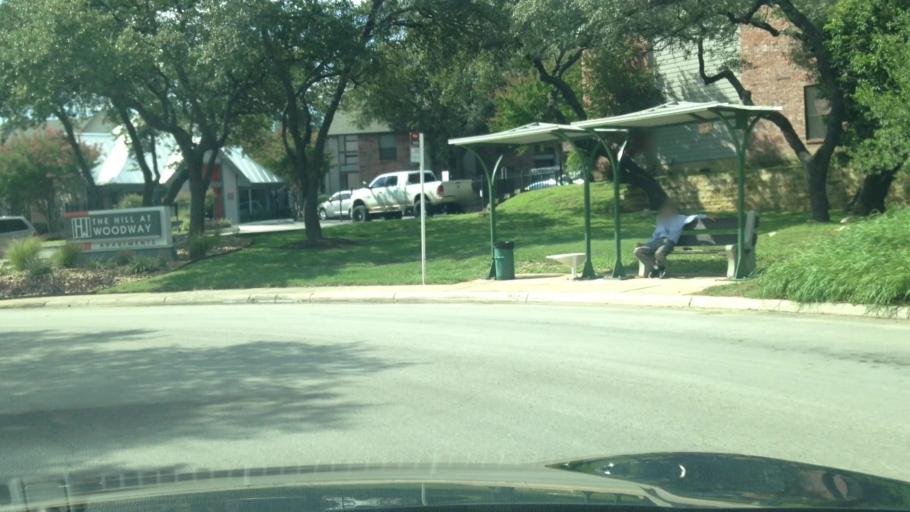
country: US
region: Texas
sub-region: Bexar County
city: Shavano Park
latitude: 29.5462
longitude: -98.5863
